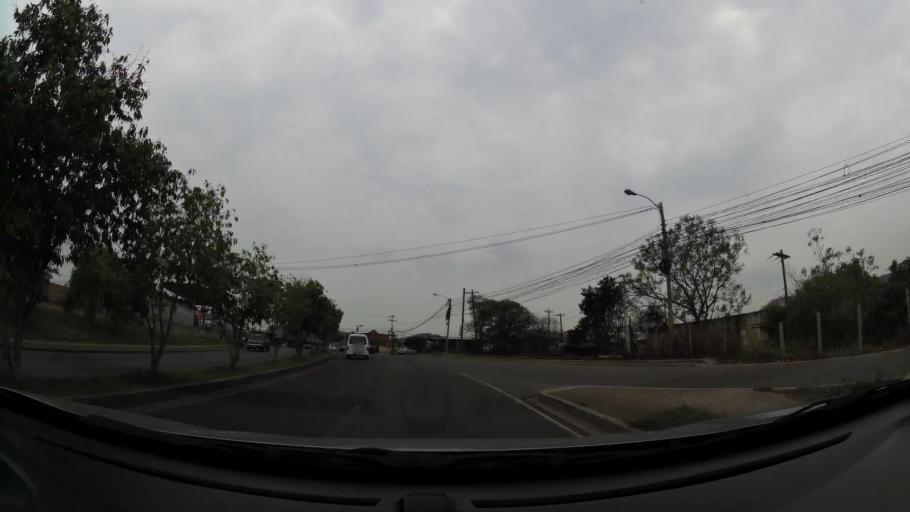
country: HN
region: Francisco Morazan
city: Yaguacire
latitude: 14.0432
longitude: -87.2234
